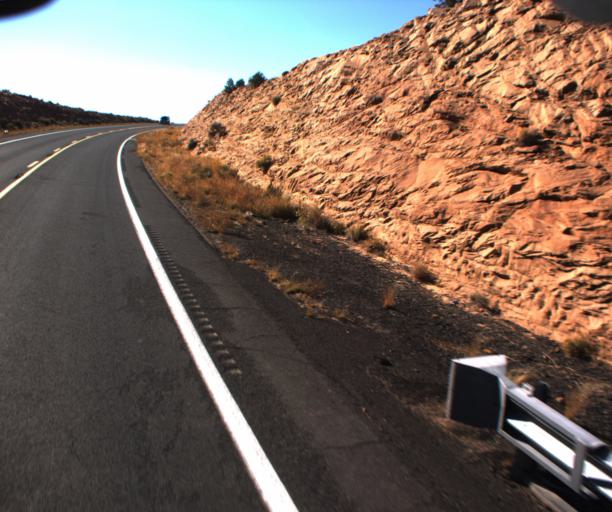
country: US
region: Arizona
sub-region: Coconino County
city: Kaibito
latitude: 36.5604
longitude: -110.7459
